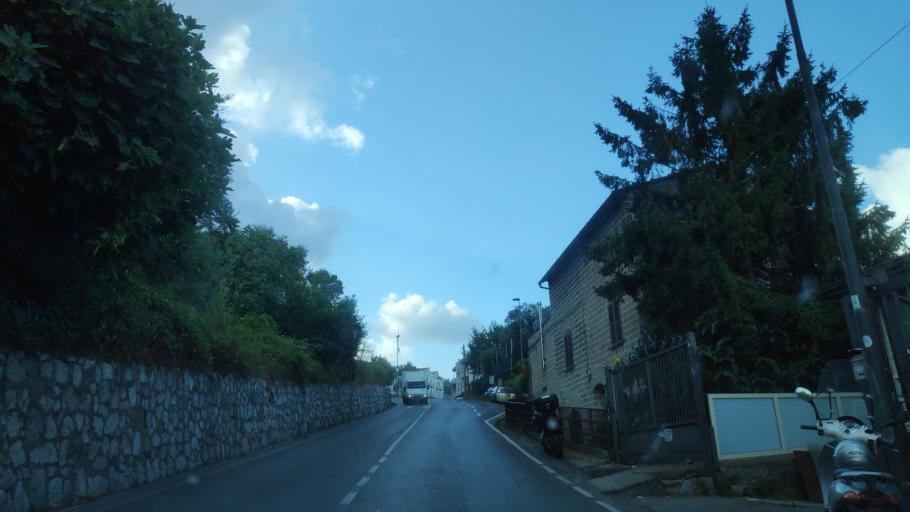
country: IT
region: Campania
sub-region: Provincia di Napoli
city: Piano di Sorrento
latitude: 40.6295
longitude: 14.4212
